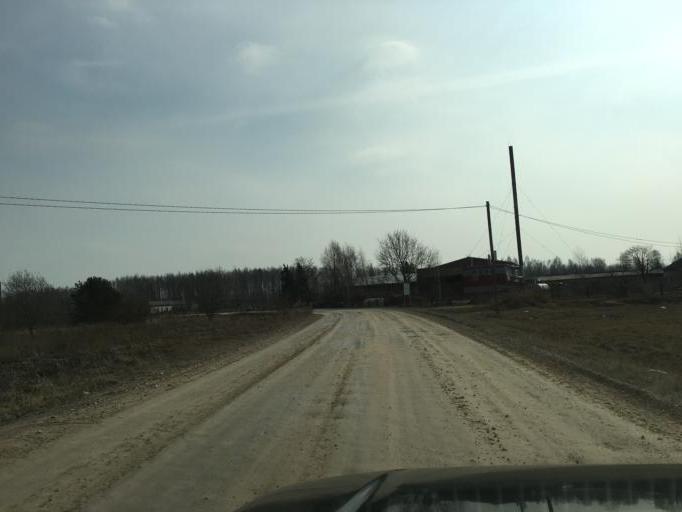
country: LV
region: Olaine
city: Olaine
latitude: 56.7956
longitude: 23.9817
